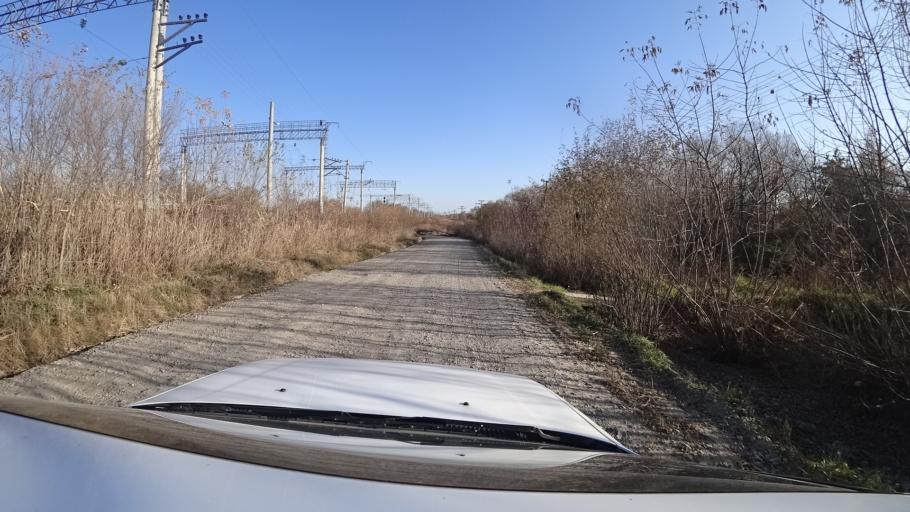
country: RU
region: Primorskiy
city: Lazo
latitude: 45.8790
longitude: 133.6478
